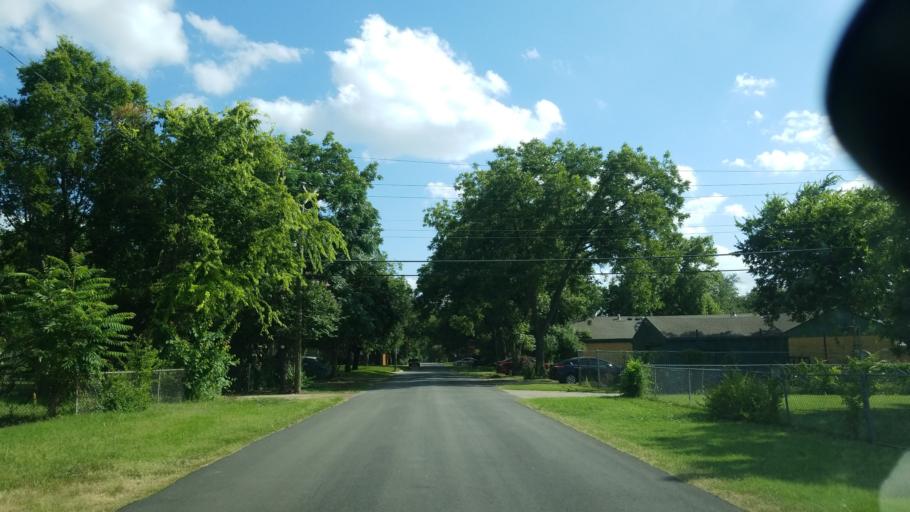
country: US
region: Texas
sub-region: Dallas County
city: Dallas
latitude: 32.7731
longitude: -96.7132
